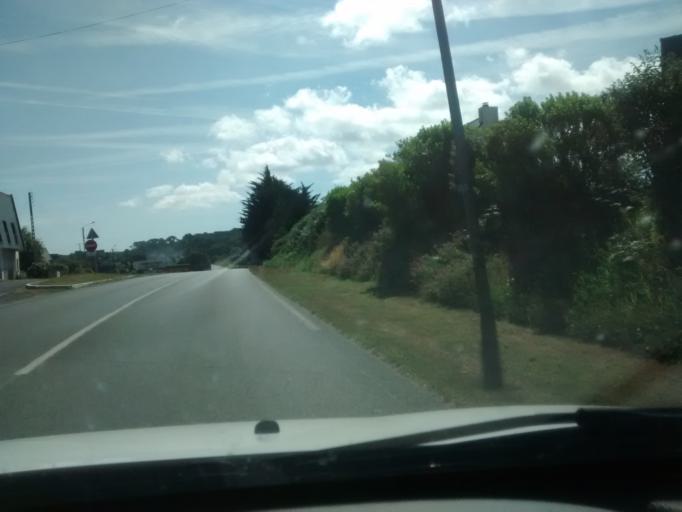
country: FR
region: Brittany
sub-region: Departement des Cotes-d'Armor
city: Trevou-Treguignec
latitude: 48.8221
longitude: -3.3456
